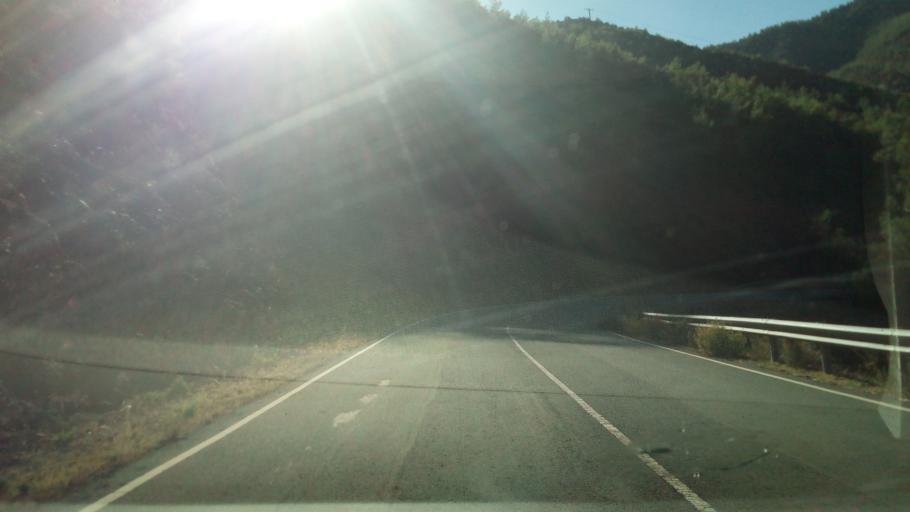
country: CY
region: Lefkosia
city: Kato Pyrgos
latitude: 35.1045
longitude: 32.7465
